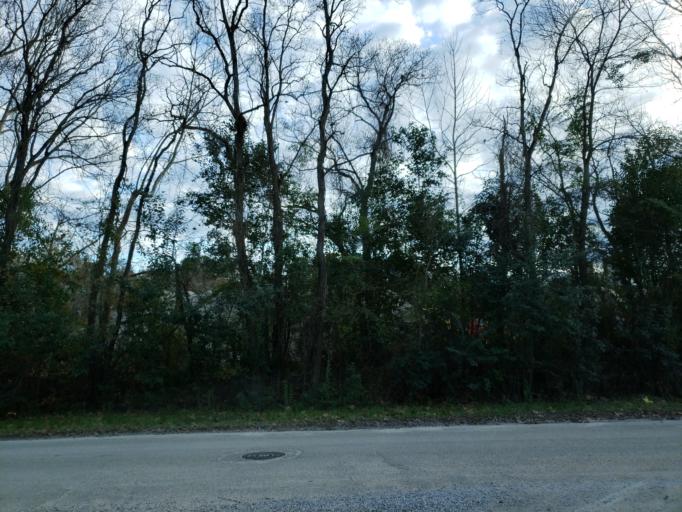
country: US
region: Mississippi
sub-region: Forrest County
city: Hattiesburg
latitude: 31.3030
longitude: -89.3192
